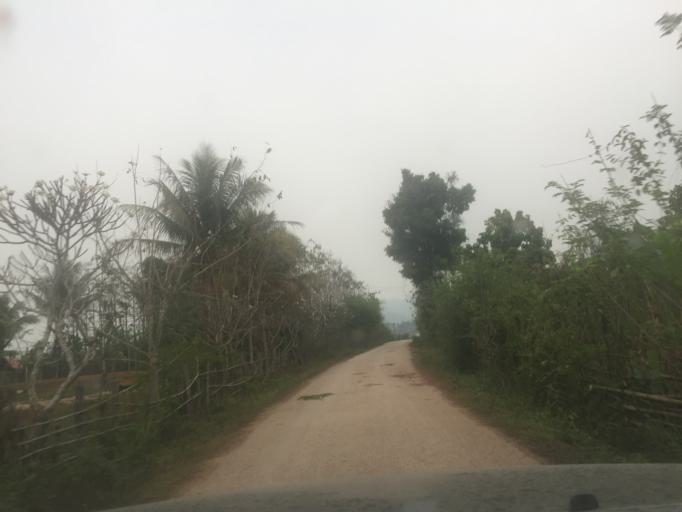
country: LA
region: Xiagnabouli
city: Sainyabuli
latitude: 19.0467
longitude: 101.5158
